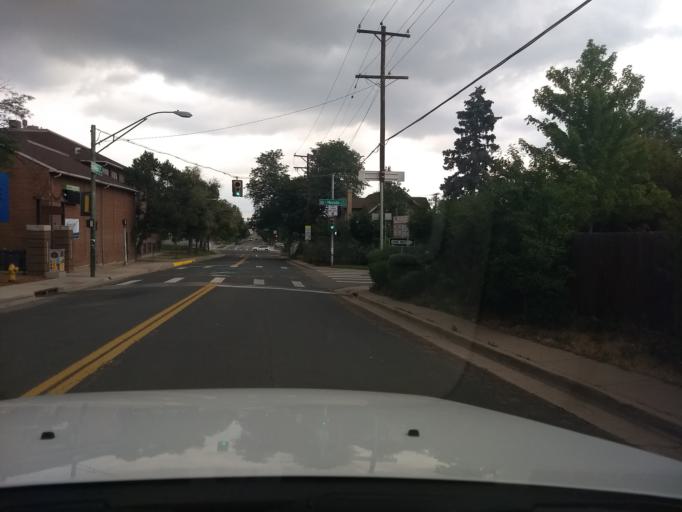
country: US
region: Colorado
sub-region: Denver County
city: Denver
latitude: 39.7100
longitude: -105.0110
